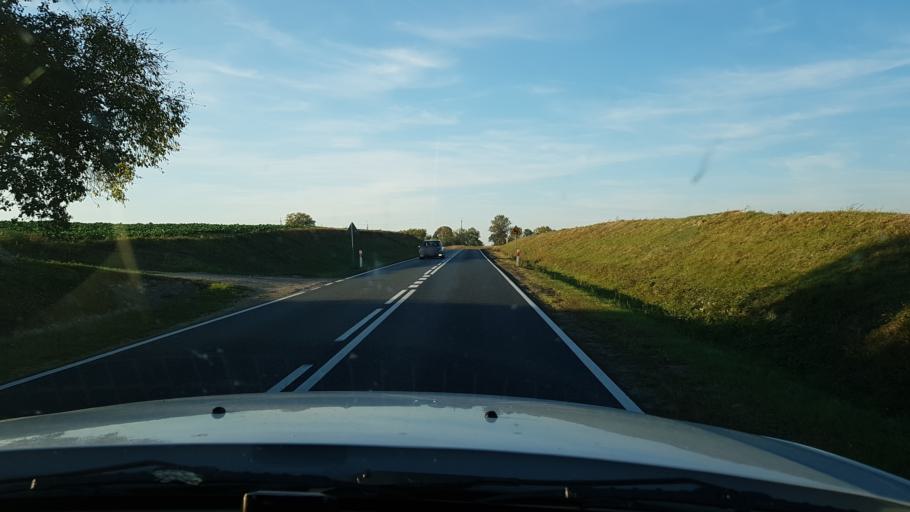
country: DE
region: Brandenburg
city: Schwedt (Oder)
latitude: 53.0267
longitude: 14.3225
